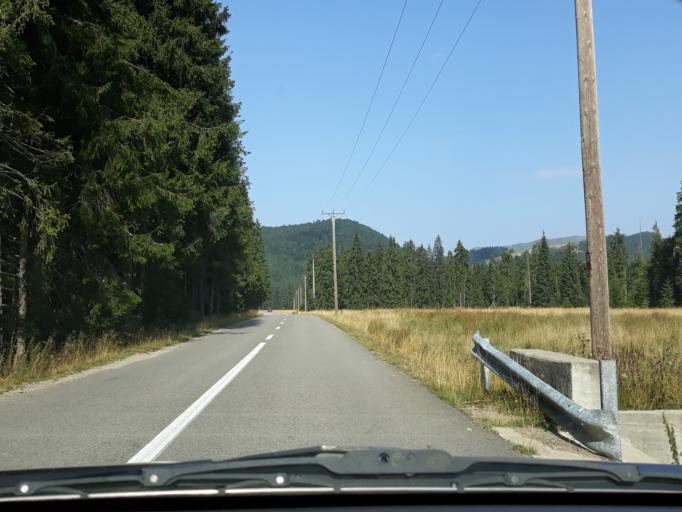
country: RO
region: Alba
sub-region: Comuna Arieseni
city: Arieseni
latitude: 46.5969
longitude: 22.7179
